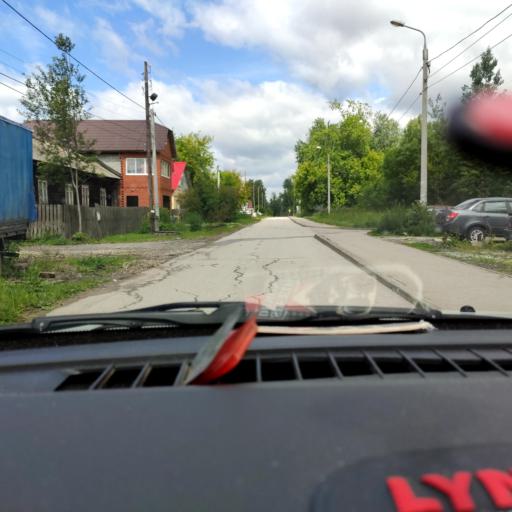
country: RU
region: Perm
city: Perm
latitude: 58.0778
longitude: 56.3584
